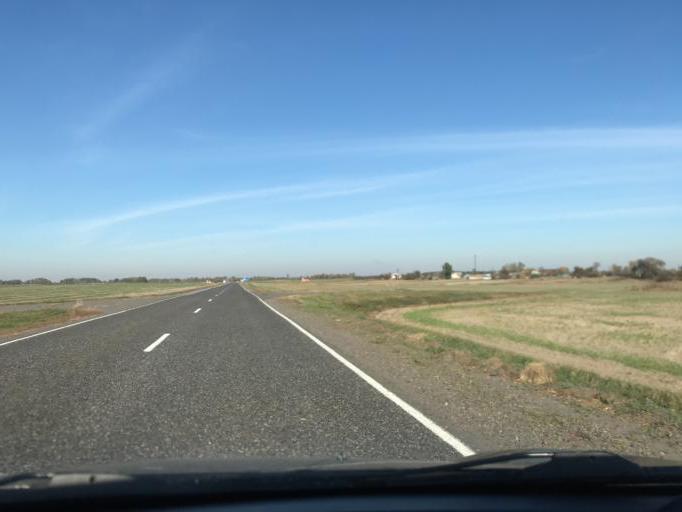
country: BY
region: Gomel
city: Brahin
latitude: 51.6635
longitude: 30.4271
